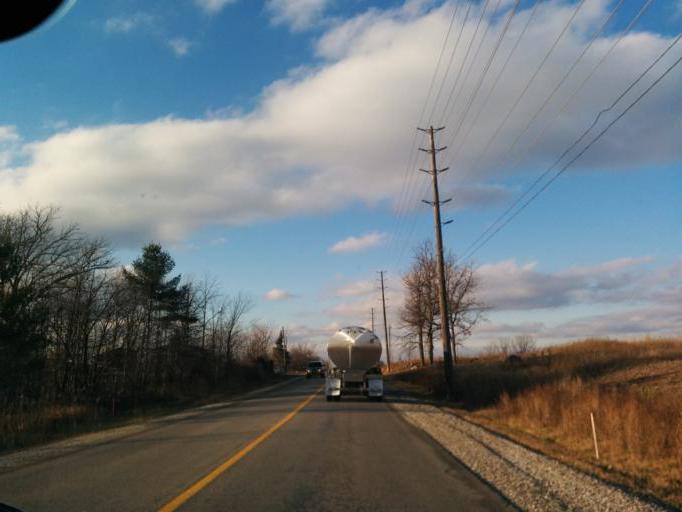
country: CA
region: Ontario
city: Oakville
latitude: 43.5178
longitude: -79.7102
